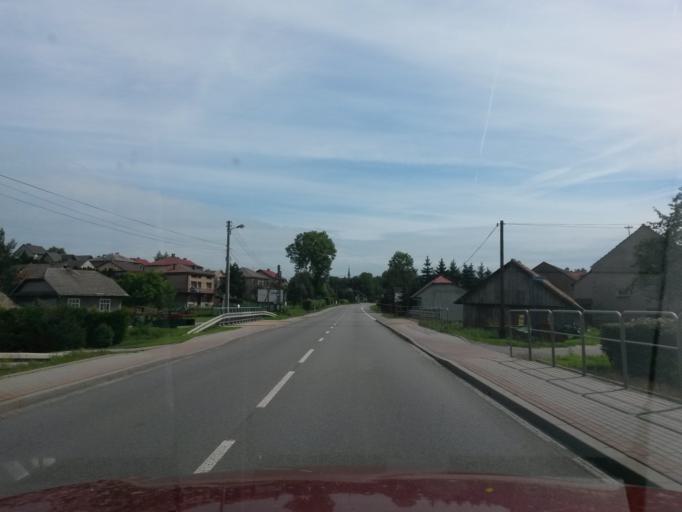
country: PL
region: Lesser Poland Voivodeship
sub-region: Powiat bochenski
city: Lapczyca
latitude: 49.9604
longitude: 20.3686
